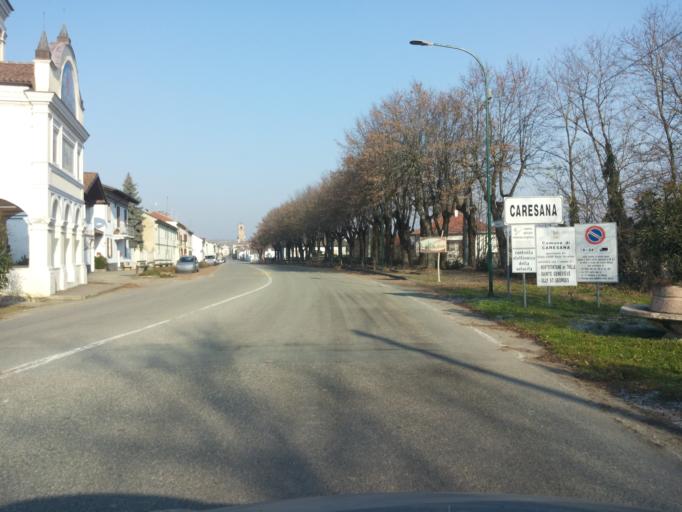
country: IT
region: Piedmont
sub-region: Provincia di Vercelli
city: Caresana
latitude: 45.2161
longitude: 8.5062
